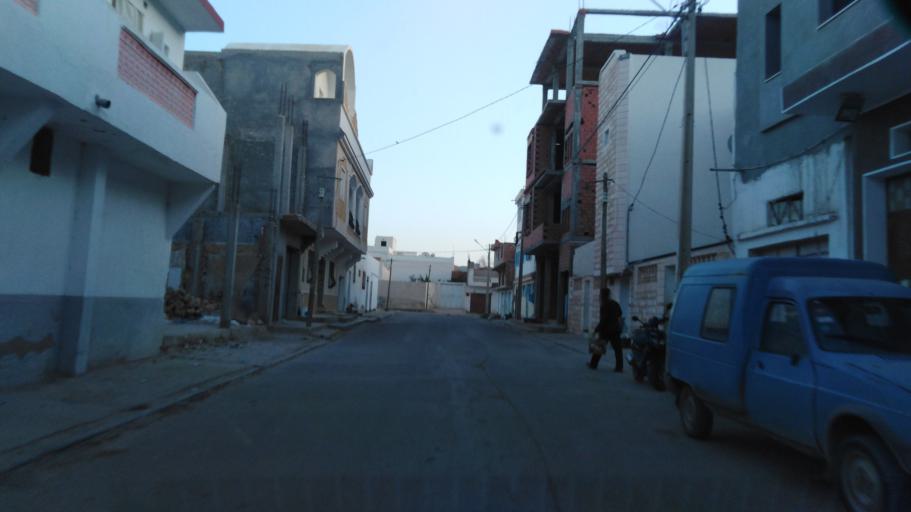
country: TN
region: Tataouine
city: Tataouine
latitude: 32.9347
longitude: 10.4535
